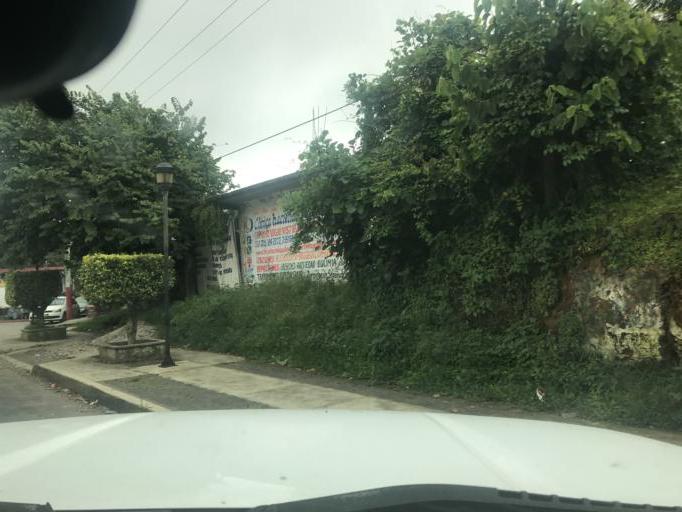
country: MX
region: Morelos
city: Ocuituco
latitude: 18.8810
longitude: -98.7744
